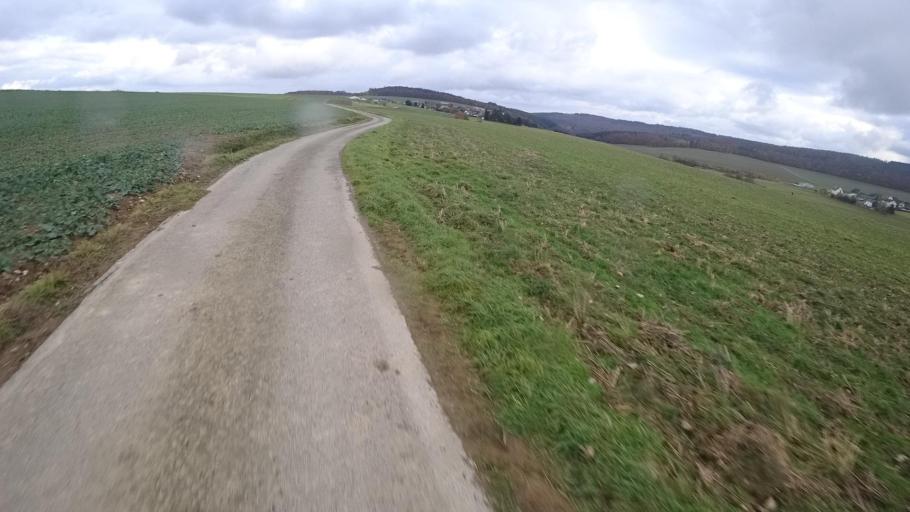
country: DE
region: Rheinland-Pfalz
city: Birkheim
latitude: 50.1241
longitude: 7.6204
